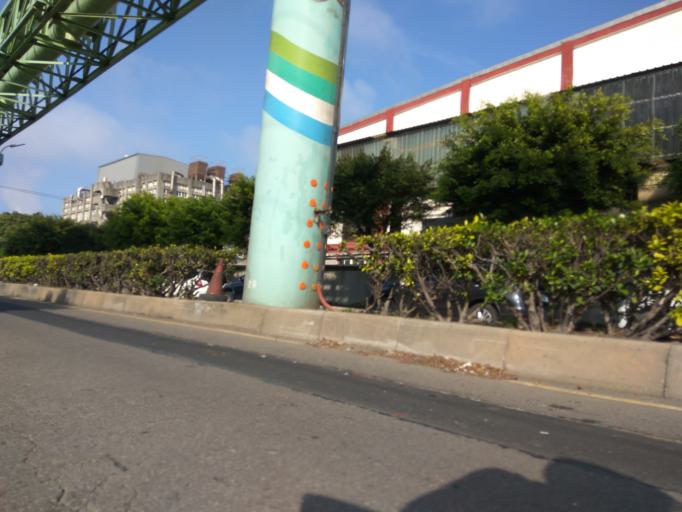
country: TW
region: Taiwan
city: Taoyuan City
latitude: 25.0734
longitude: 121.1768
